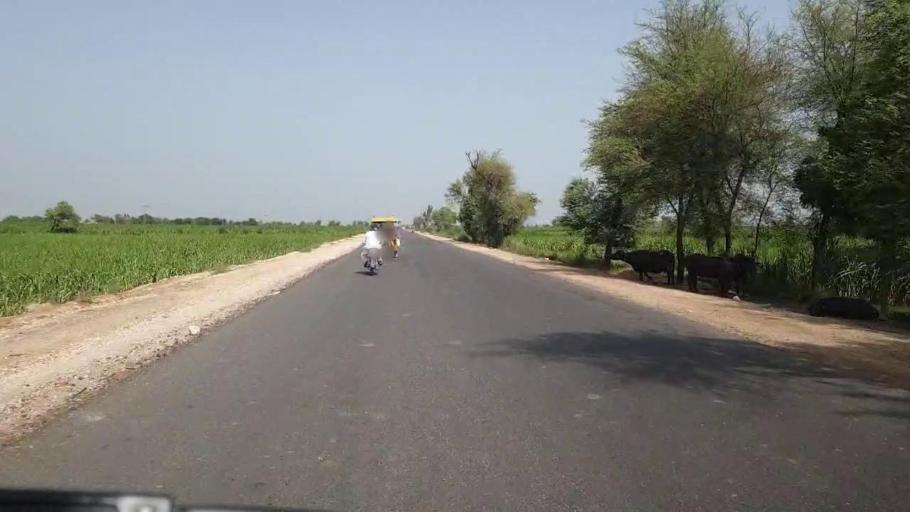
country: PK
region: Sindh
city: Sakrand
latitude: 26.2716
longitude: 68.1599
